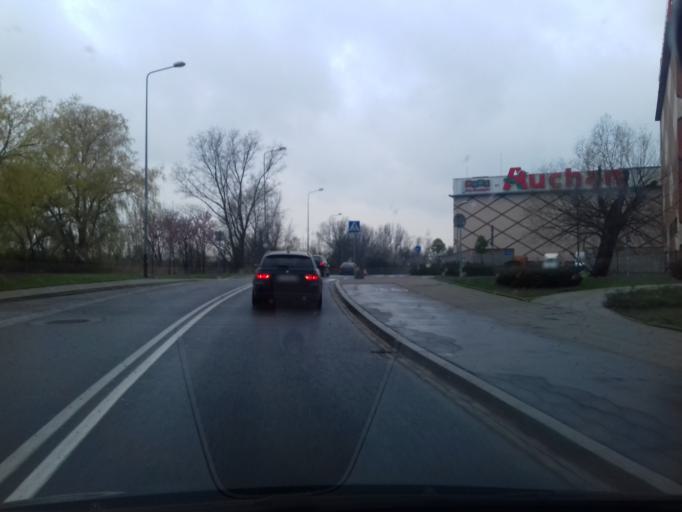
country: PL
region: Lesser Poland Voivodeship
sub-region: Krakow
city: Krakow
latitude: 50.0262
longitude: 19.9494
